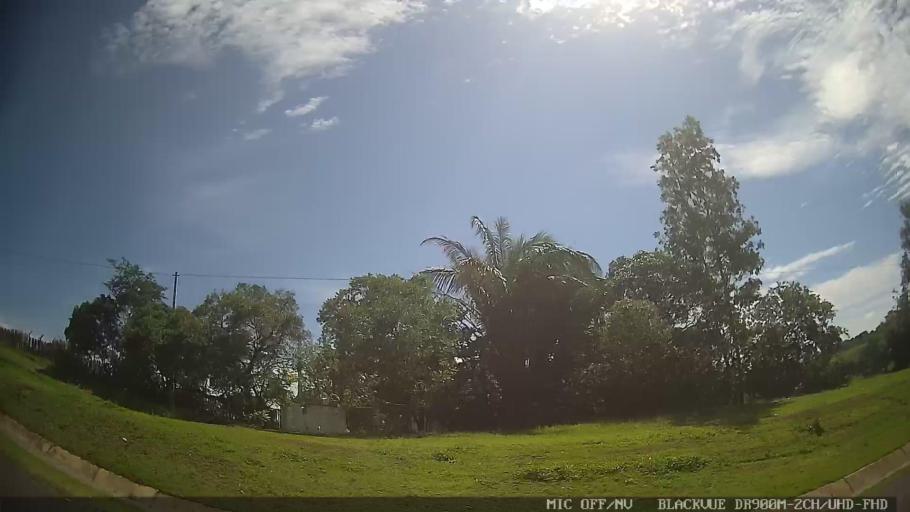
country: BR
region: Sao Paulo
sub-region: Tiete
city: Tiete
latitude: -23.1588
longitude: -47.6502
